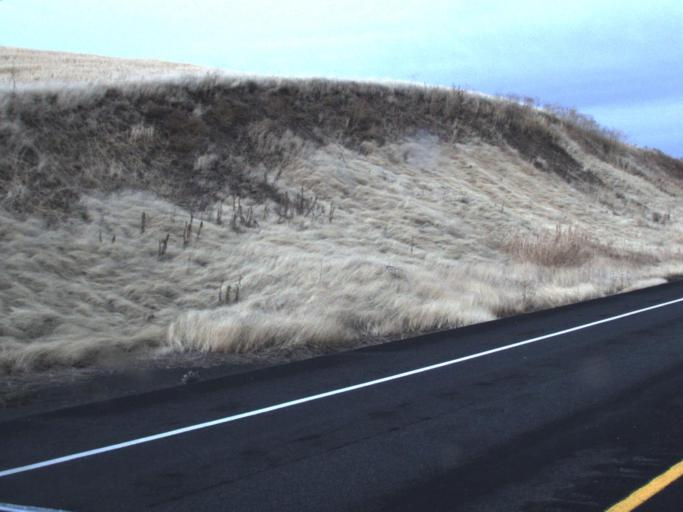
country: US
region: Washington
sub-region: Whitman County
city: Pullman
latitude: 46.6370
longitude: -117.1769
